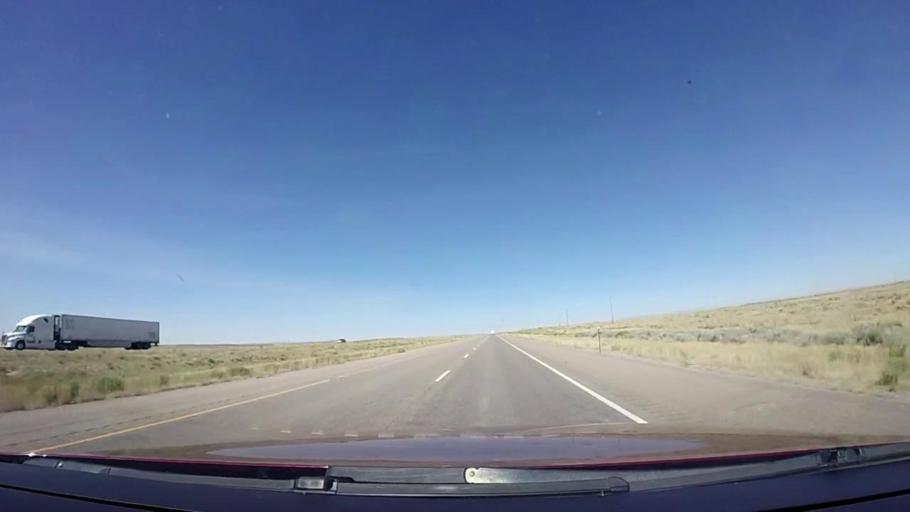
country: US
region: Wyoming
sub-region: Sweetwater County
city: Rock Springs
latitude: 41.6382
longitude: -108.4523
